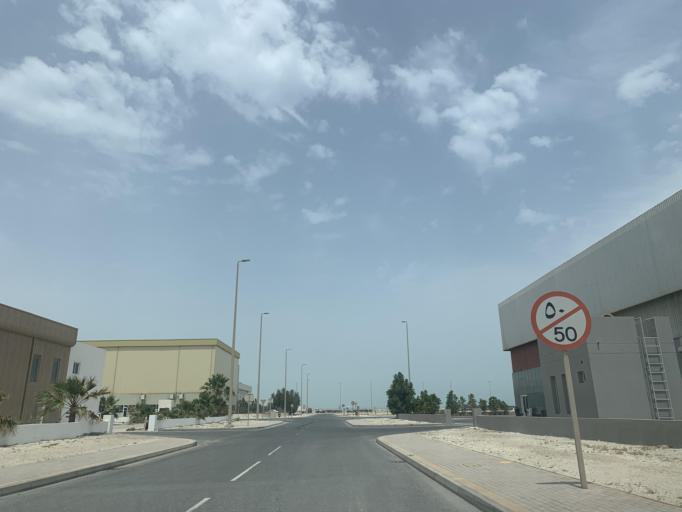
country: BH
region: Muharraq
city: Al Hadd
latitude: 26.2224
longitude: 50.6832
